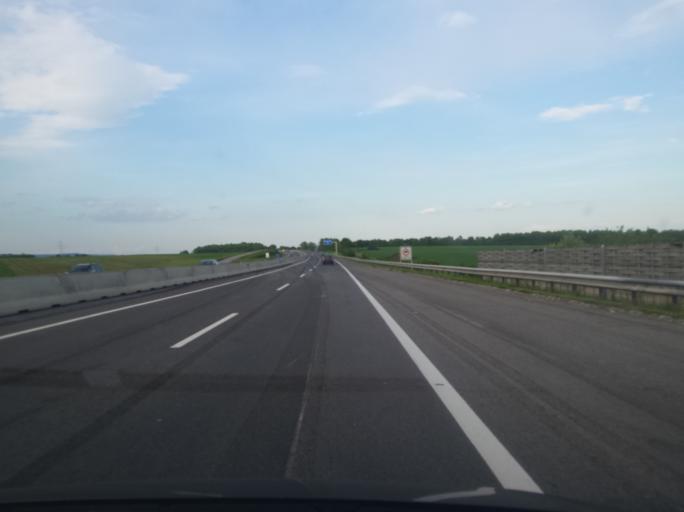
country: AT
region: Burgenland
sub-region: Politischer Bezirk Mattersburg
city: Hirm
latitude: 47.7980
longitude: 16.4603
